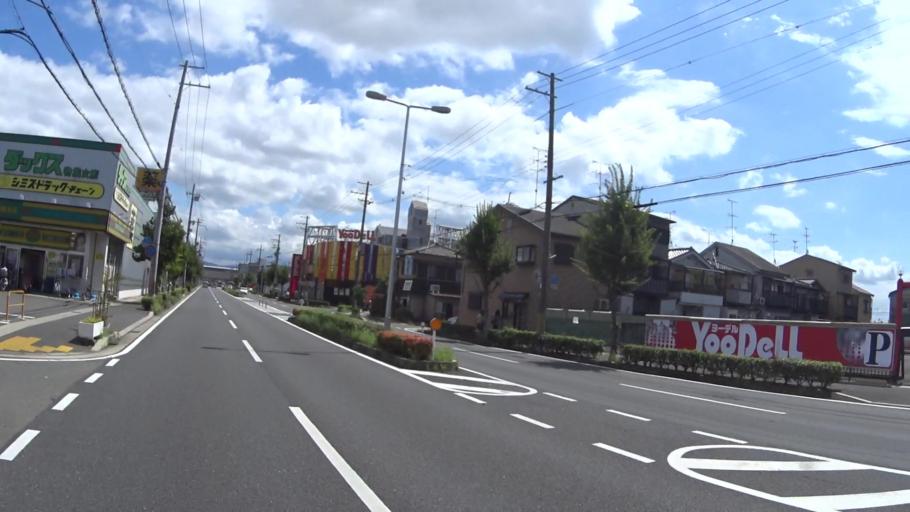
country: JP
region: Kyoto
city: Muko
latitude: 34.9644
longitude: 135.6985
